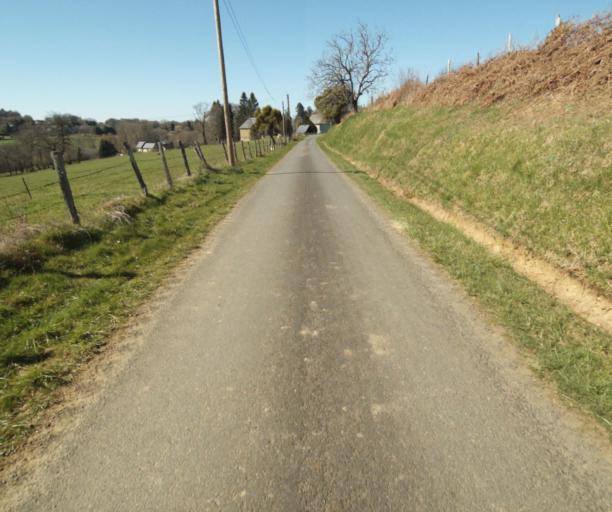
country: FR
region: Limousin
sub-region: Departement de la Correze
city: Chamboulive
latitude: 45.3959
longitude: 1.6548
